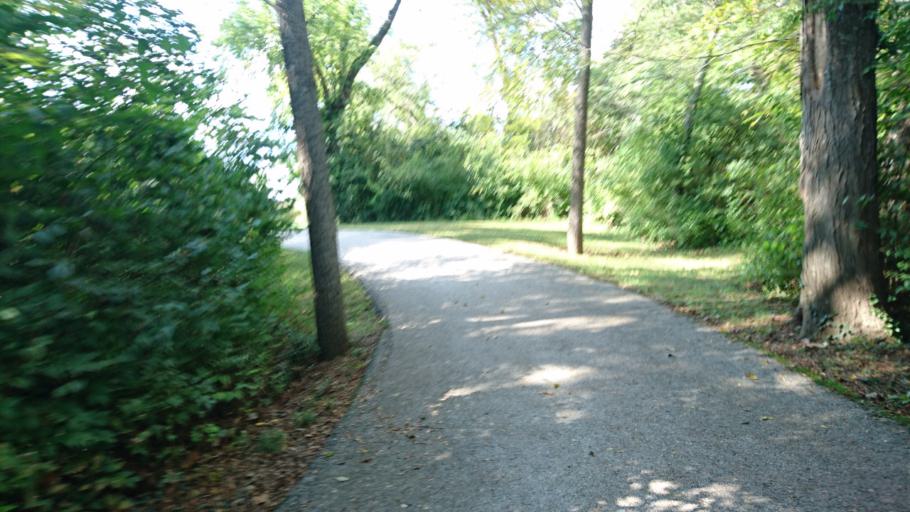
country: US
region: Missouri
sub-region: Saint Louis County
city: Eureka
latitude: 38.5481
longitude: -90.6310
